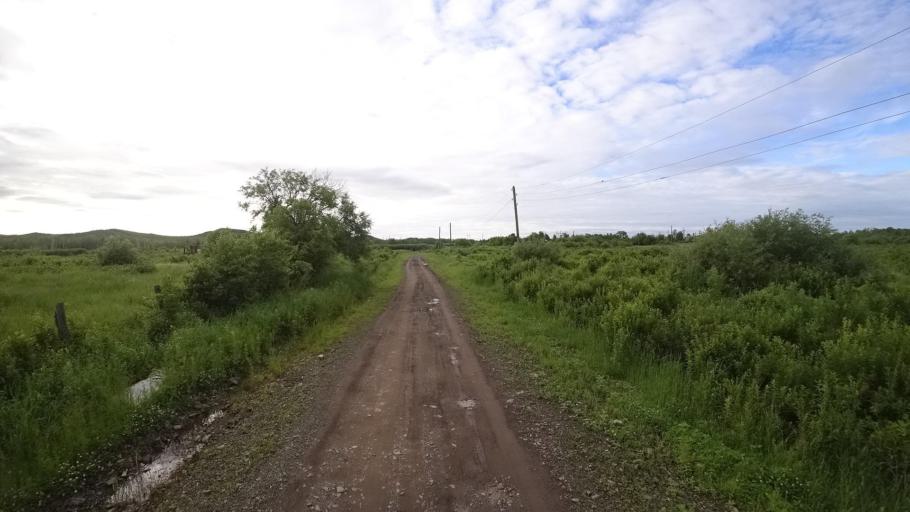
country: RU
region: Khabarovsk Krai
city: Amursk
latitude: 49.8854
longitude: 136.1280
